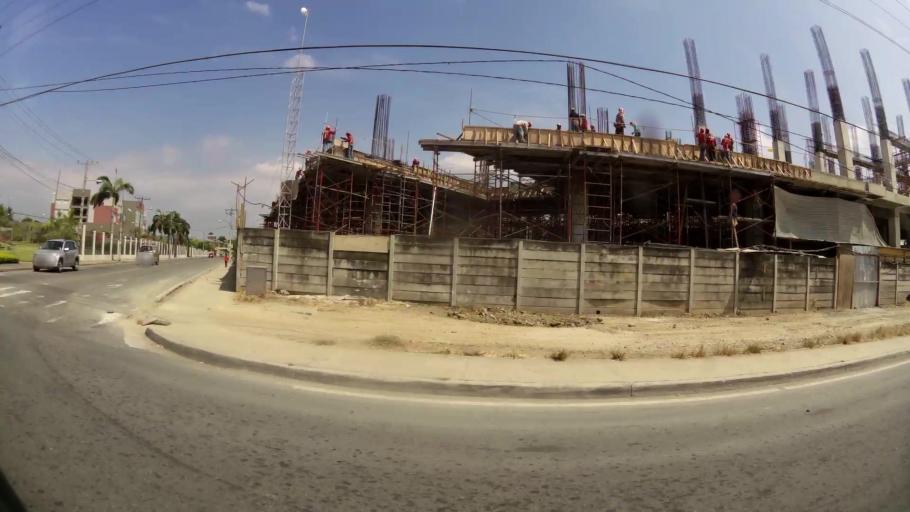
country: EC
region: Guayas
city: Eloy Alfaro
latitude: -2.1323
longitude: -79.8633
